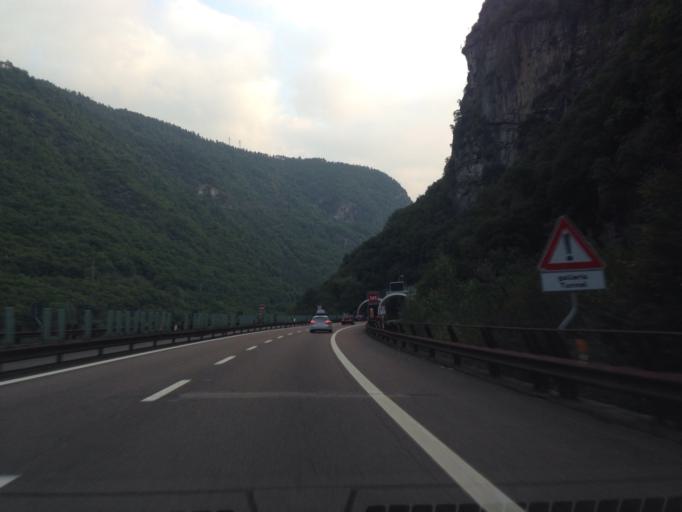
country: IT
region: Trentino-Alto Adige
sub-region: Bolzano
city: Fie Allo Sciliar
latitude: 46.5568
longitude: 11.5132
